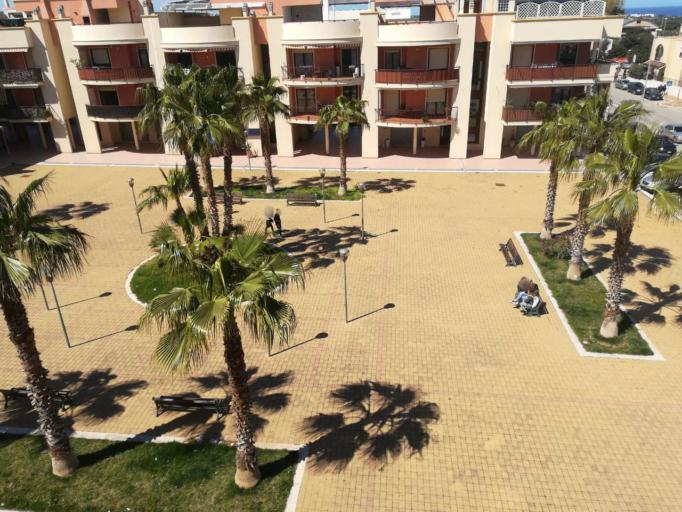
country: IT
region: Apulia
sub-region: Provincia di Bari
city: Polignano a Mare
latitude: 40.9930
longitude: 17.2124
